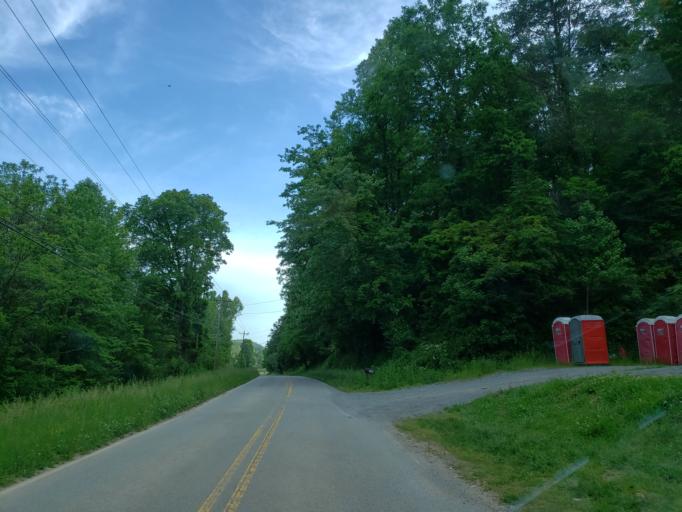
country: US
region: Georgia
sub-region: Fannin County
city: Blue Ridge
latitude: 34.8315
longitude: -84.3523
